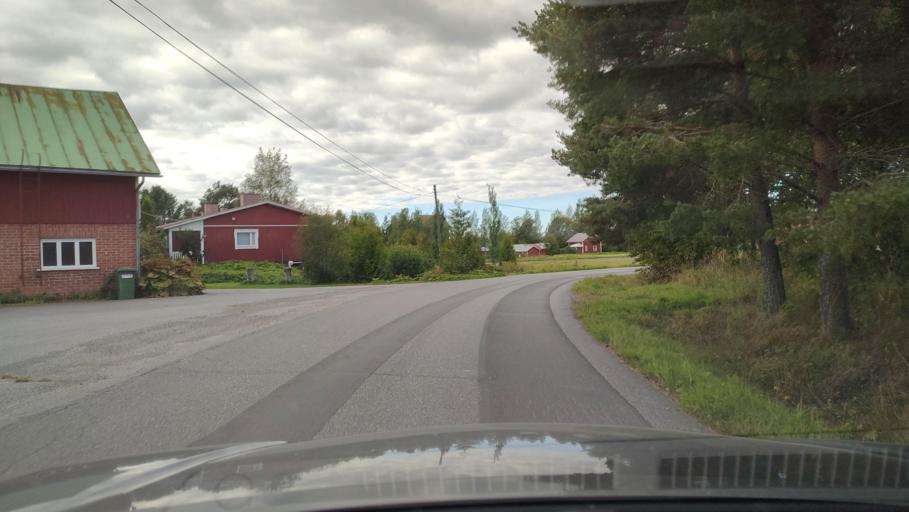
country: FI
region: Southern Ostrobothnia
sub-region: Suupohja
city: Karijoki
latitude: 62.2370
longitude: 21.5801
